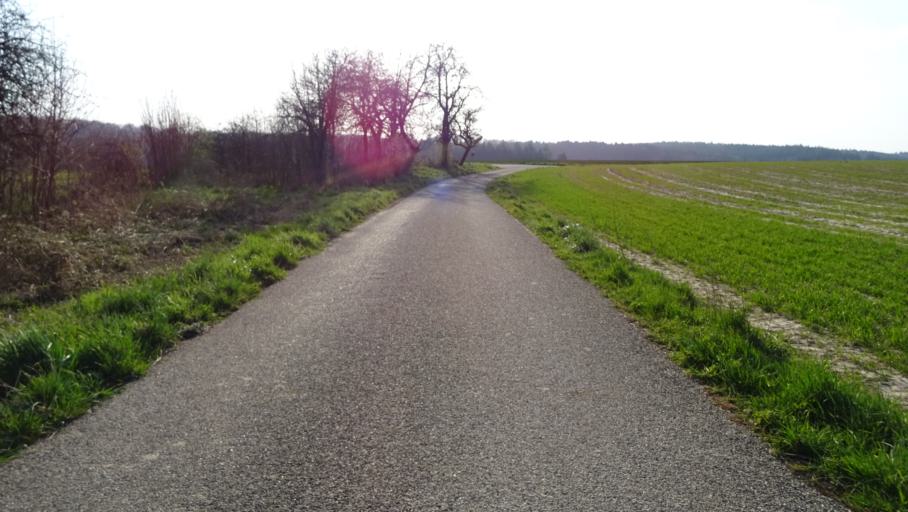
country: DE
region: Baden-Wuerttemberg
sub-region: Regierungsbezirk Stuttgart
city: Roigheim
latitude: 49.3819
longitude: 9.3536
